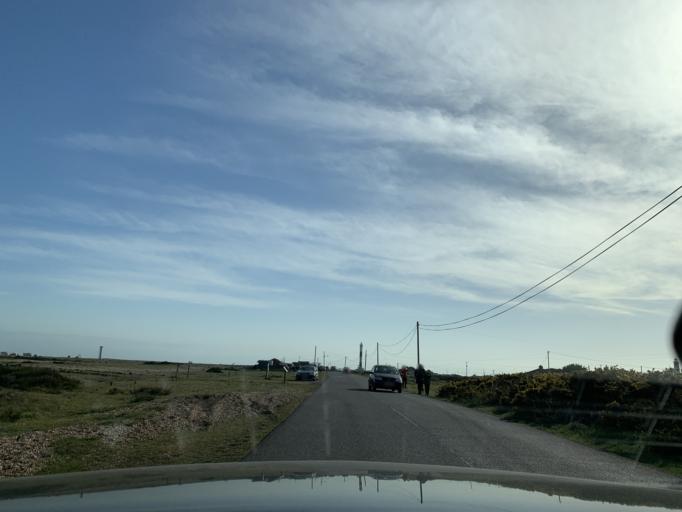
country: GB
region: England
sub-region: Kent
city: New Romney
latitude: 50.9204
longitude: 0.9768
